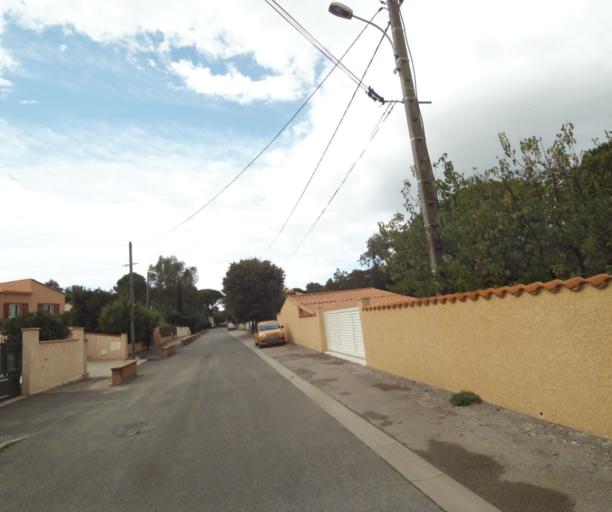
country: FR
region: Languedoc-Roussillon
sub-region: Departement des Pyrenees-Orientales
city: Argelers
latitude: 42.5435
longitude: 3.0176
